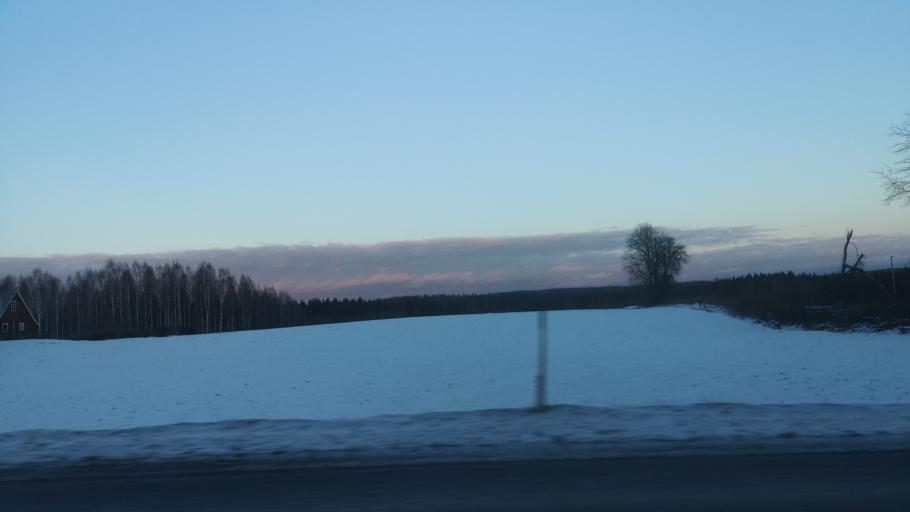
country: FI
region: Southern Savonia
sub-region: Savonlinna
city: Sulkava
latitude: 61.9128
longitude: 28.5940
